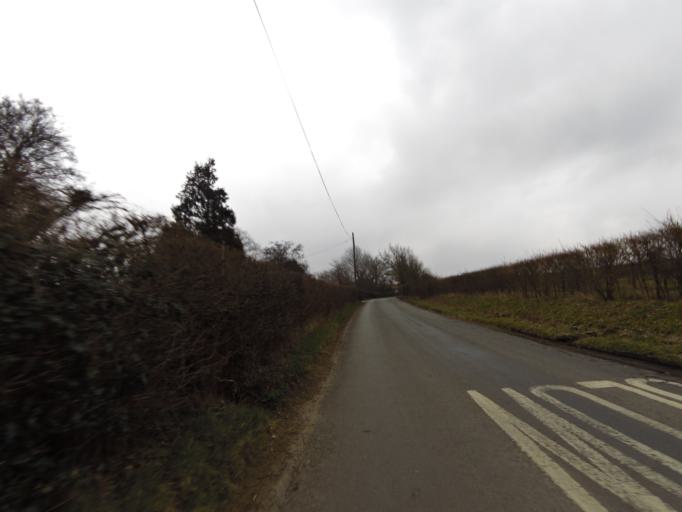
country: GB
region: England
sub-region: Suffolk
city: Framlingham
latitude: 52.1907
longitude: 1.3349
